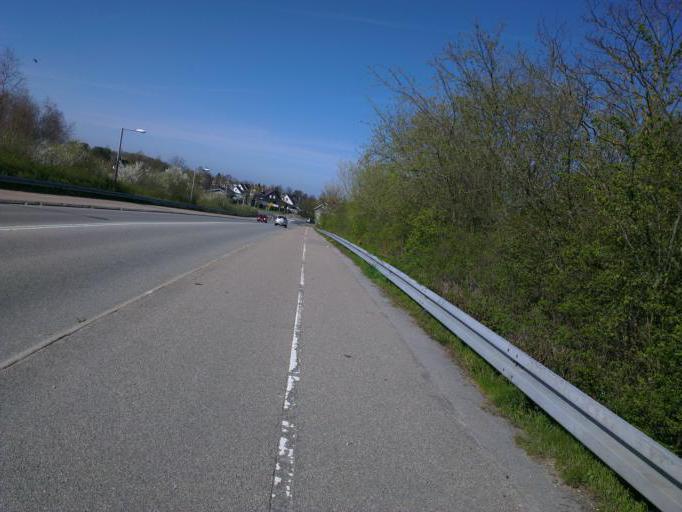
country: DK
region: Capital Region
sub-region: Frederikssund Kommune
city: Frederikssund
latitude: 55.8225
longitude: 12.0773
